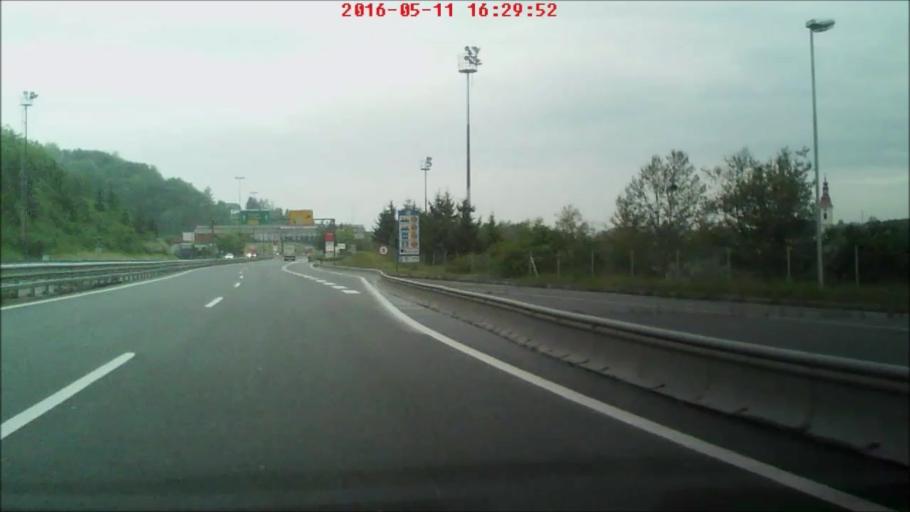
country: SI
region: Sentilj
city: Sentilj v Slov. Goricah
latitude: 46.6894
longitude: 15.6463
